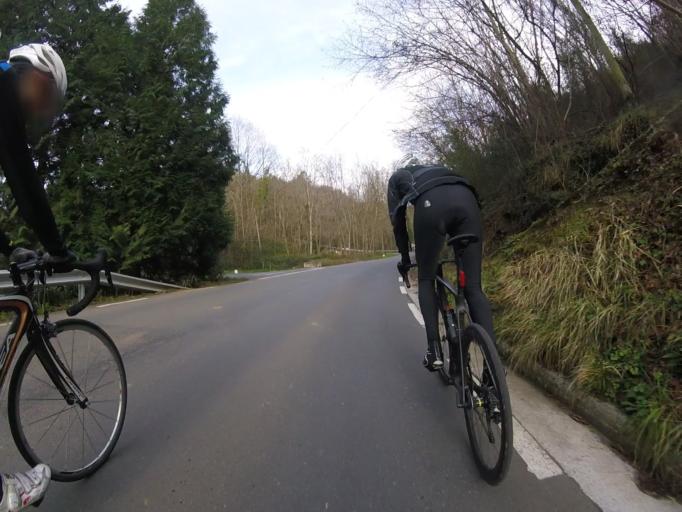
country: ES
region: Basque Country
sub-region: Provincia de Guipuzcoa
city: Anoeta
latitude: 43.1639
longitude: -2.0776
